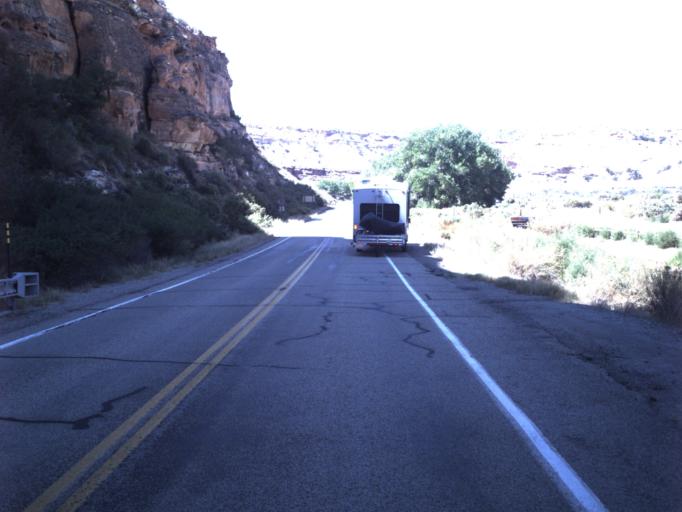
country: US
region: Utah
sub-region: Grand County
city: Moab
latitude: 38.8104
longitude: -109.3067
